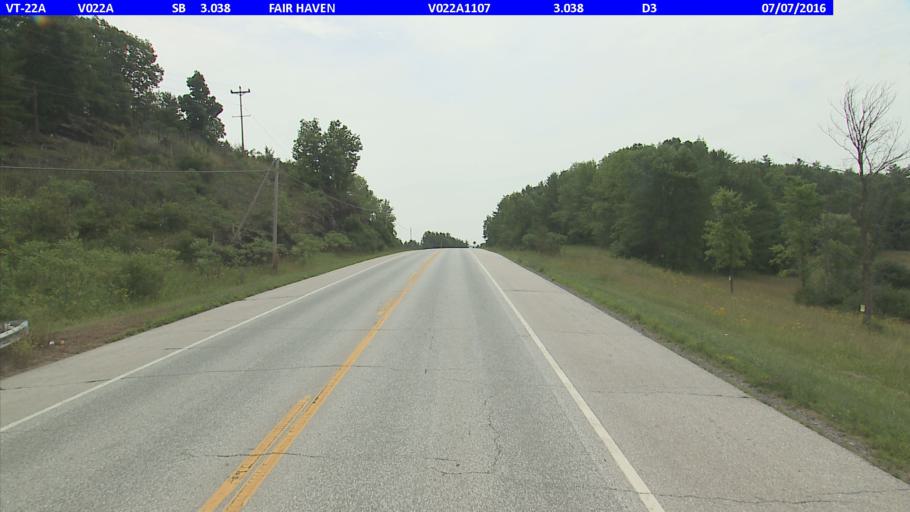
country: US
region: Vermont
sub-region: Rutland County
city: Fair Haven
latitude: 43.6112
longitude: -73.2847
